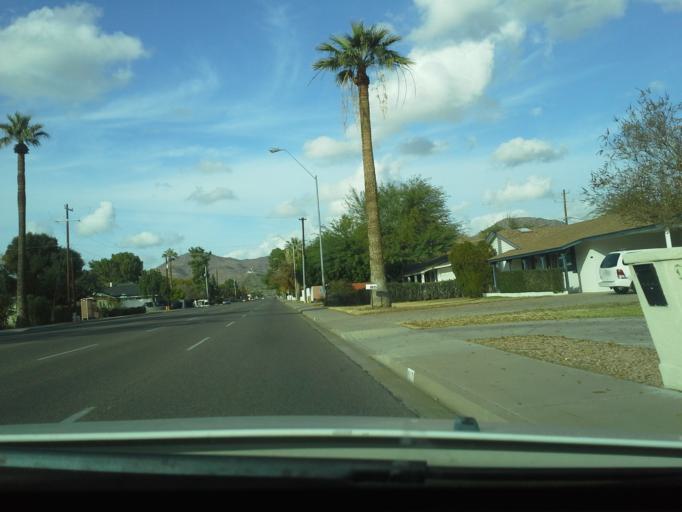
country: US
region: Arizona
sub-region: Maricopa County
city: Glendale
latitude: 33.5623
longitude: -112.0824
